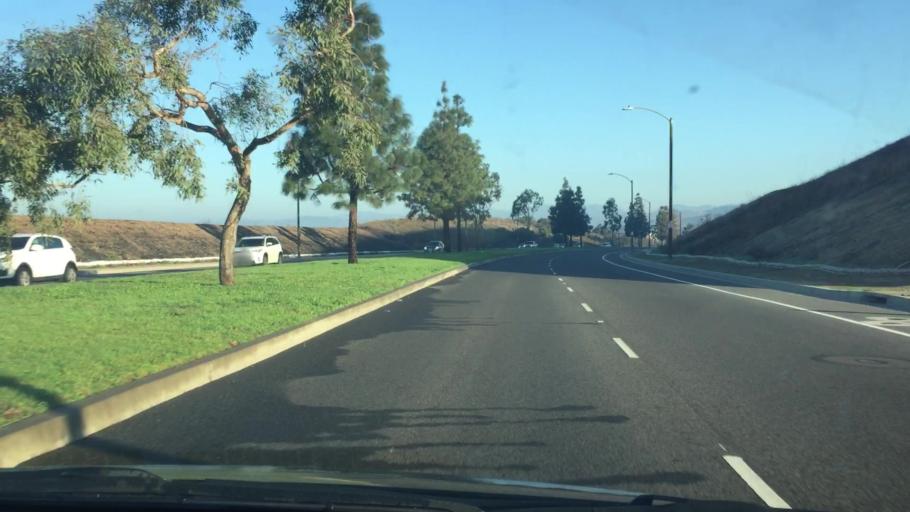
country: US
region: California
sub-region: Orange County
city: North Tustin
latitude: 33.7771
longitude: -117.7592
